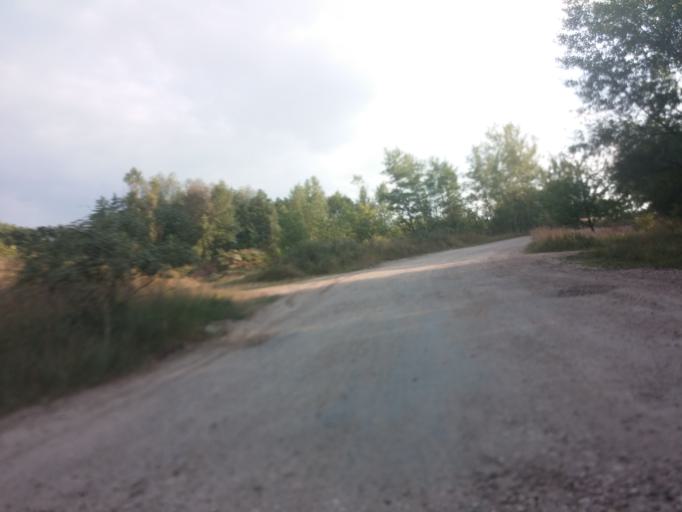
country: CZ
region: Central Bohemia
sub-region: Okres Nymburk
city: Podebrady
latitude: 50.1280
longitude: 15.1228
